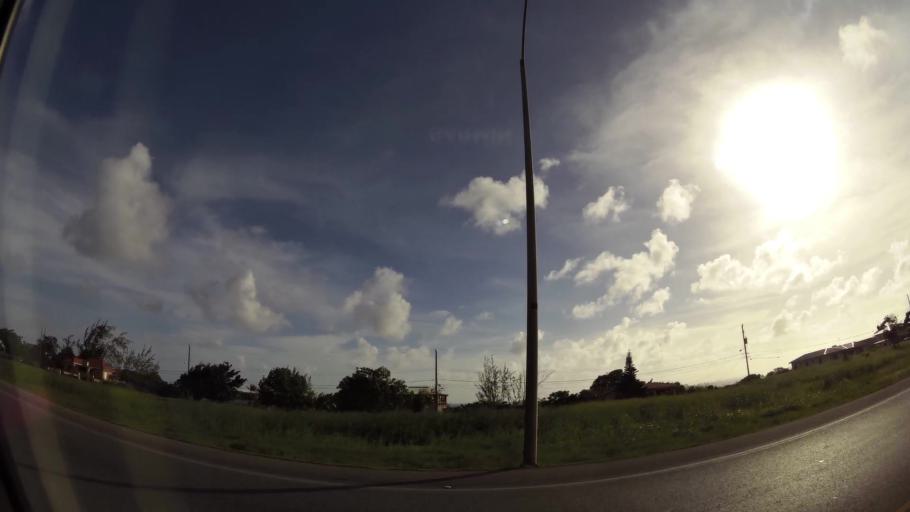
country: BB
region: Christ Church
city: Oistins
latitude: 13.0767
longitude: -59.5668
